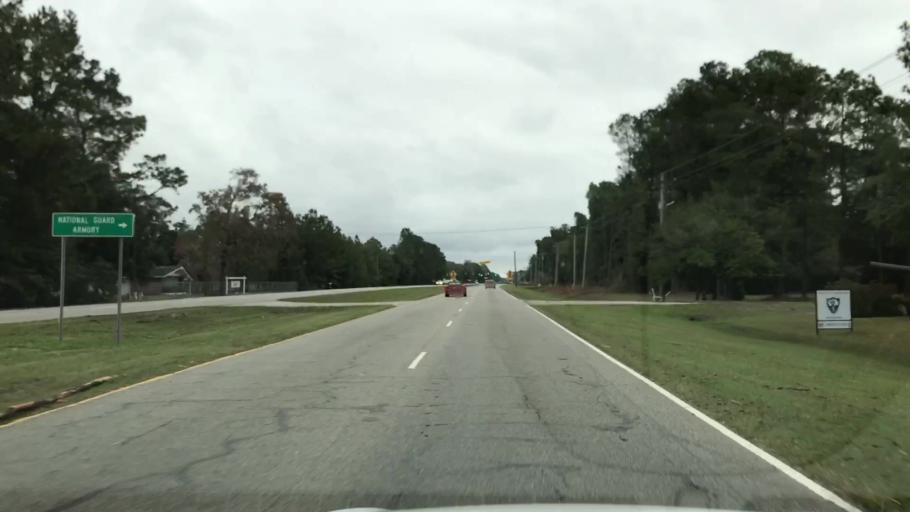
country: US
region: South Carolina
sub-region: Georgetown County
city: Georgetown
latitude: 33.3230
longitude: -79.3197
